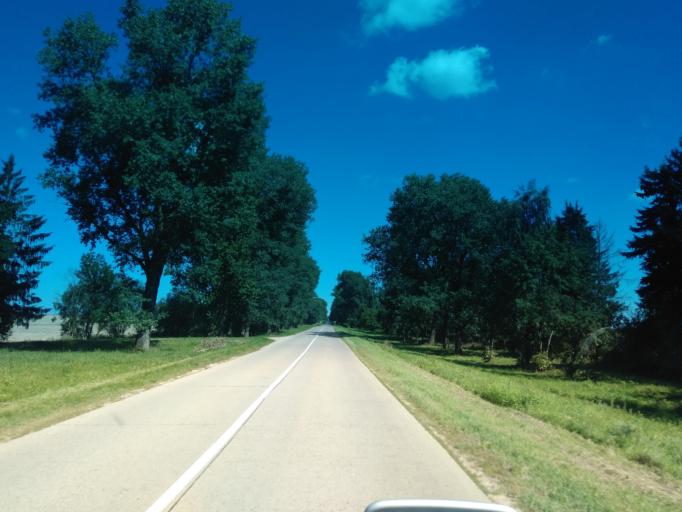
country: BY
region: Minsk
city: Stan'kava
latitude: 53.6540
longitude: 27.3136
